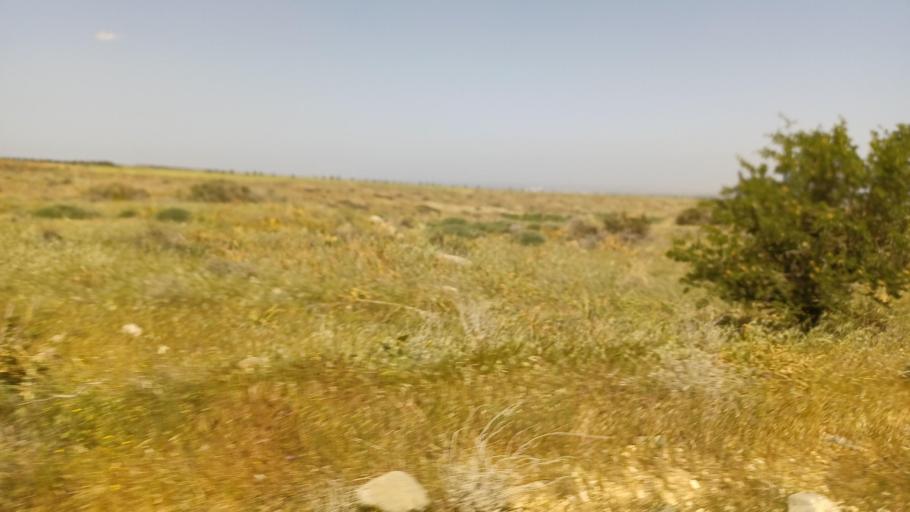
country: CY
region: Lefkosia
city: Lefka
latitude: 35.0998
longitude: 32.9381
